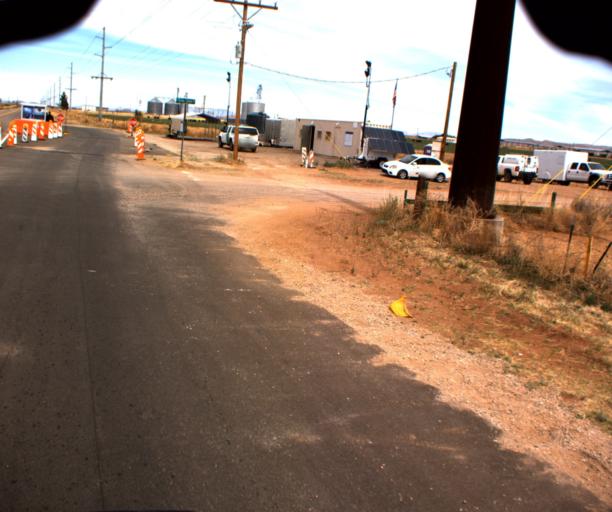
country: US
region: Arizona
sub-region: Cochise County
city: Tombstone
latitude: 31.7584
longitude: -109.6894
